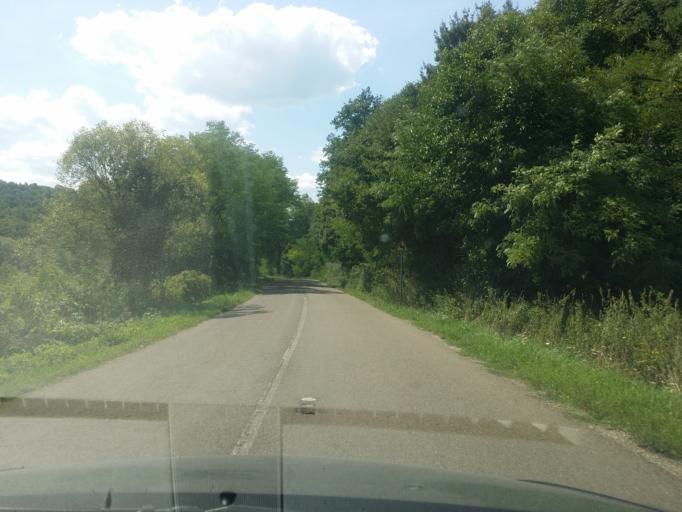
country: HU
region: Pest
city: Veroce
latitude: 47.8335
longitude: 19.0761
